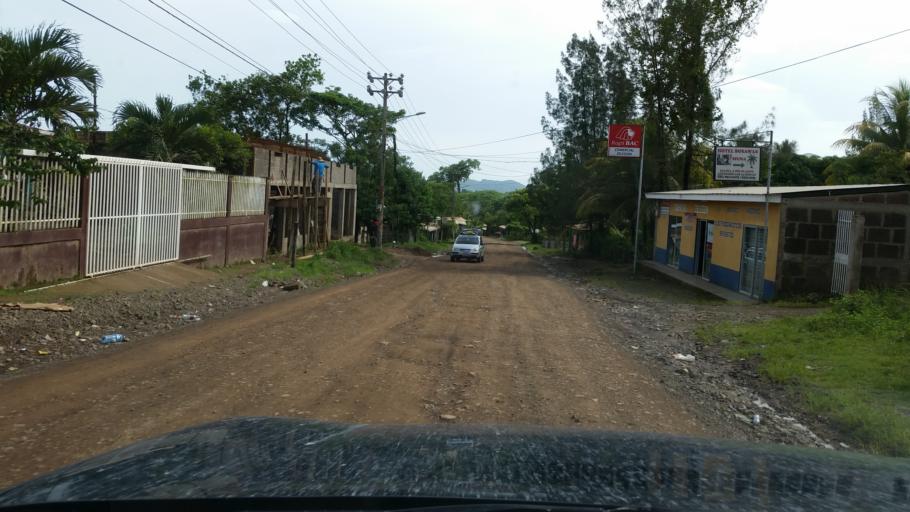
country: NI
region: Atlantico Norte (RAAN)
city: Siuna
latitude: 13.7145
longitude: -84.7735
